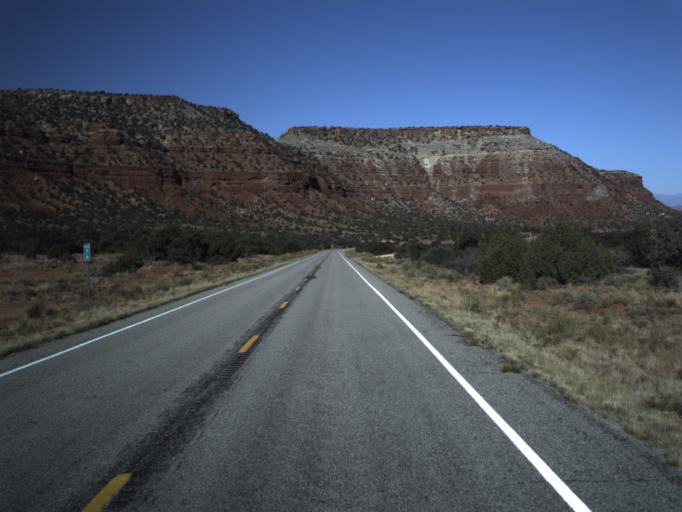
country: US
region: Utah
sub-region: San Juan County
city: Blanding
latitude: 37.6337
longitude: -110.0978
